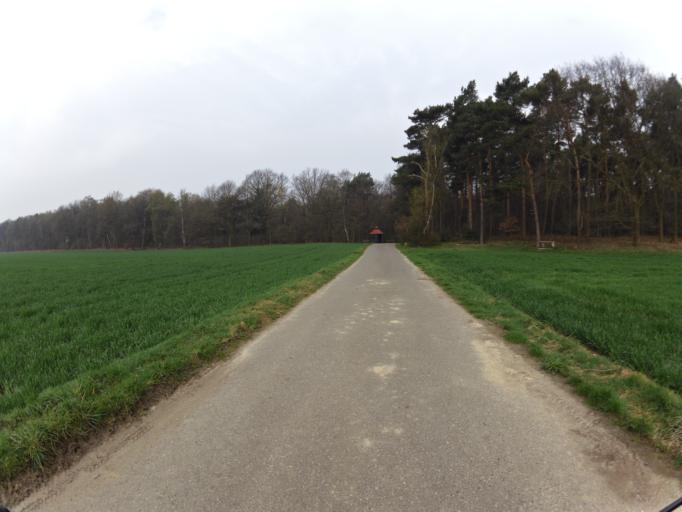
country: DE
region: North Rhine-Westphalia
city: Geilenkirchen
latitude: 50.9735
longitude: 6.0617
